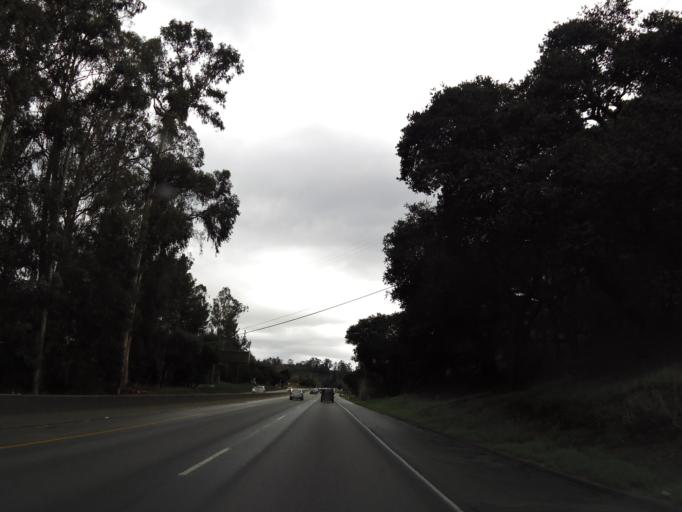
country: US
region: California
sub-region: Monterey County
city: Prunedale
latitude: 36.8100
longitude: -121.6447
